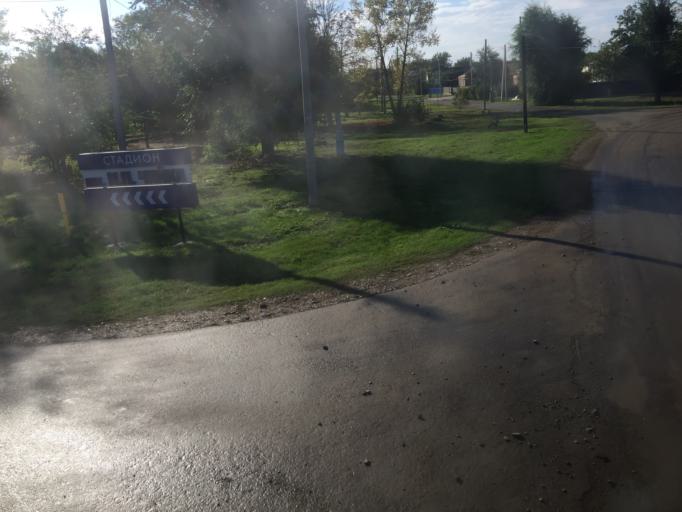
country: RU
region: Rostov
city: Peschanokopskoye
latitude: 46.1897
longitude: 41.0823
